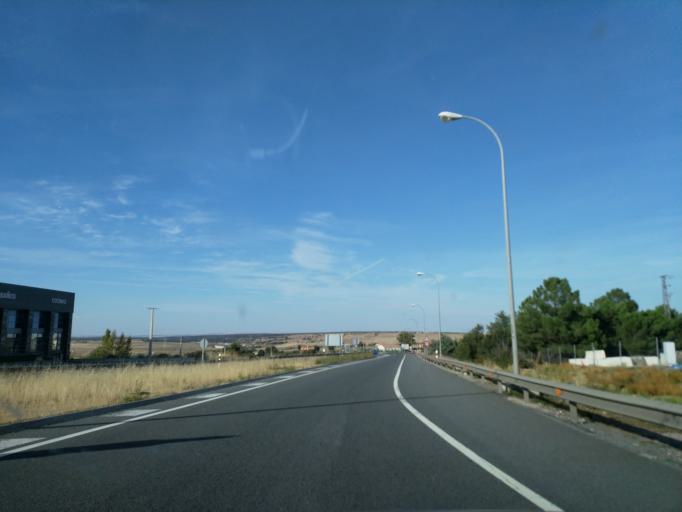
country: ES
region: Castille and Leon
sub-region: Provincia de Segovia
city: Villacastin
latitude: 40.7735
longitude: -4.4253
